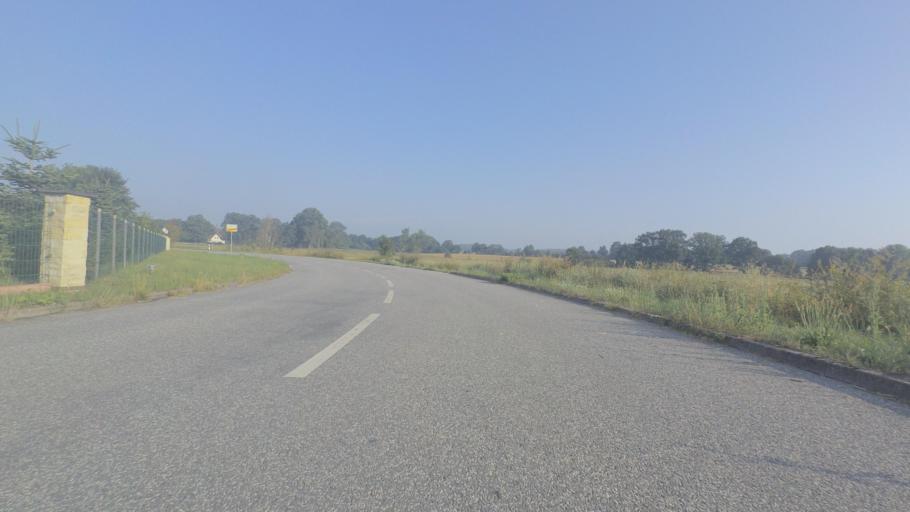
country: DE
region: Brandenburg
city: Heiligengrabe
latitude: 53.2442
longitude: 12.3569
